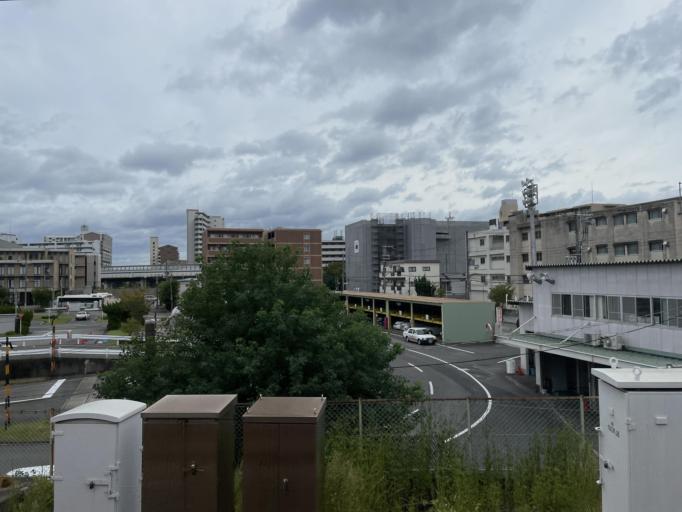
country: JP
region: Hyogo
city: Nishinomiya-hama
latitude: 34.7409
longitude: 135.3570
